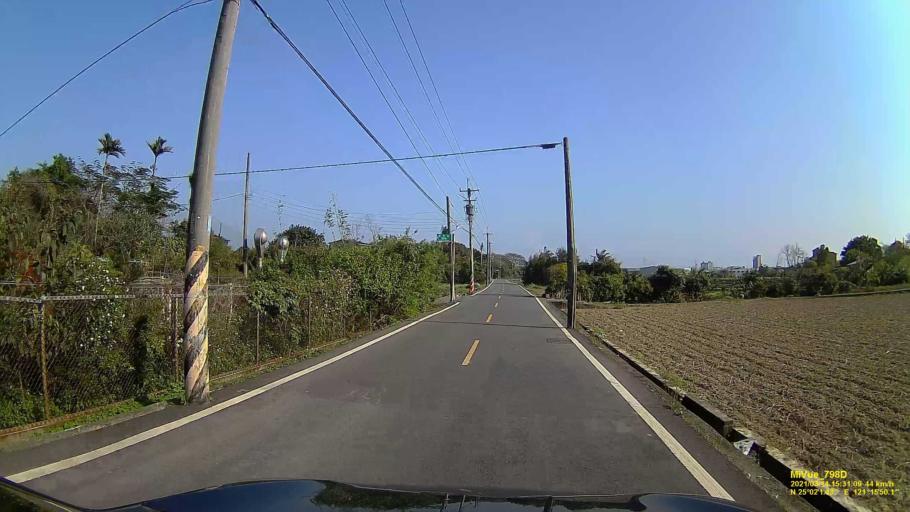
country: TW
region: Taiwan
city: Taoyuan City
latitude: 25.0336
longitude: 121.2640
